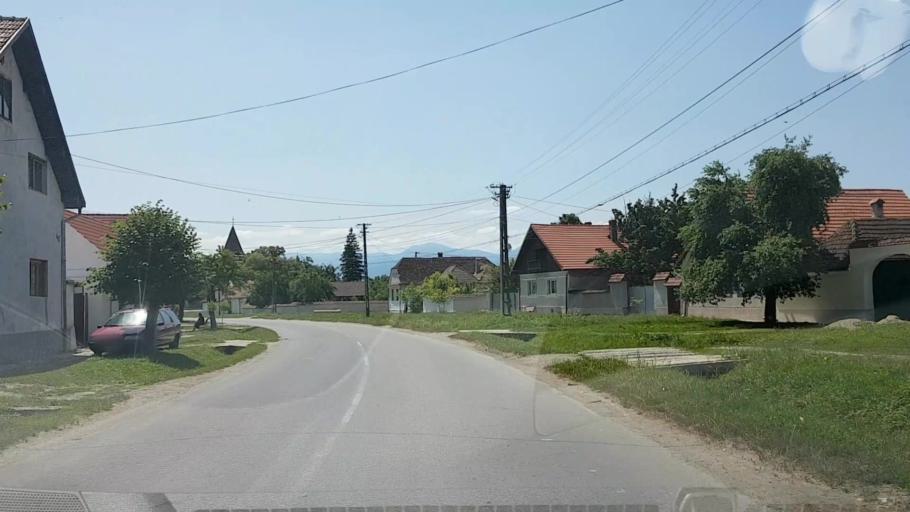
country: RO
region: Brasov
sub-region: Comuna Voila
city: Voila
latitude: 45.8386
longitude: 24.8327
